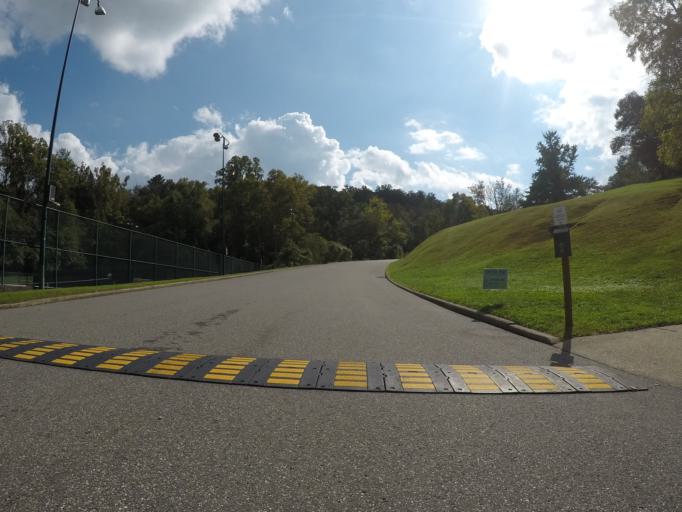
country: US
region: West Virginia
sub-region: Cabell County
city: Huntington
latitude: 38.4060
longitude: -82.4344
